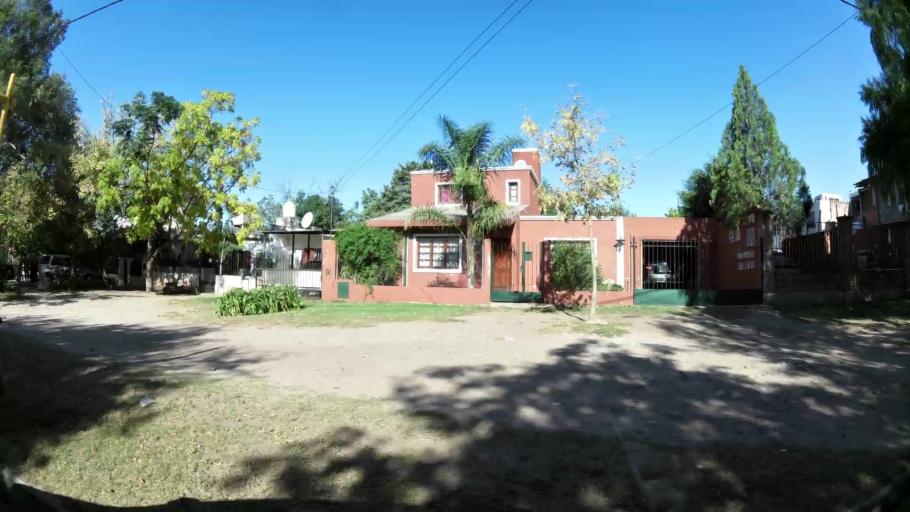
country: AR
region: Cordoba
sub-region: Departamento de Capital
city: Cordoba
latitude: -31.3758
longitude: -64.2488
